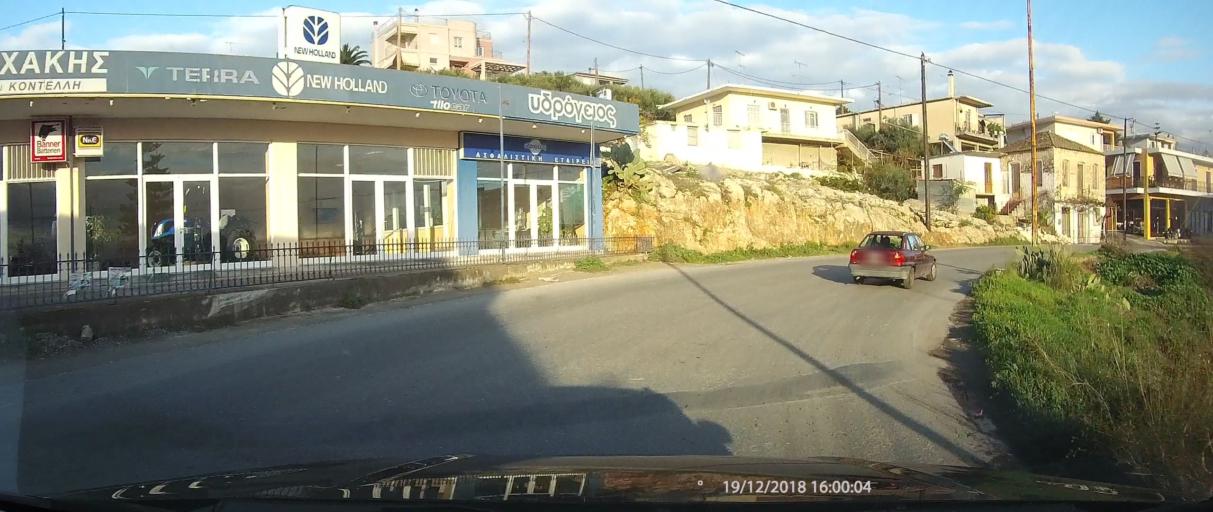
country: GR
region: Peloponnese
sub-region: Nomos Lakonias
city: Skala
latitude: 36.8552
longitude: 22.6756
